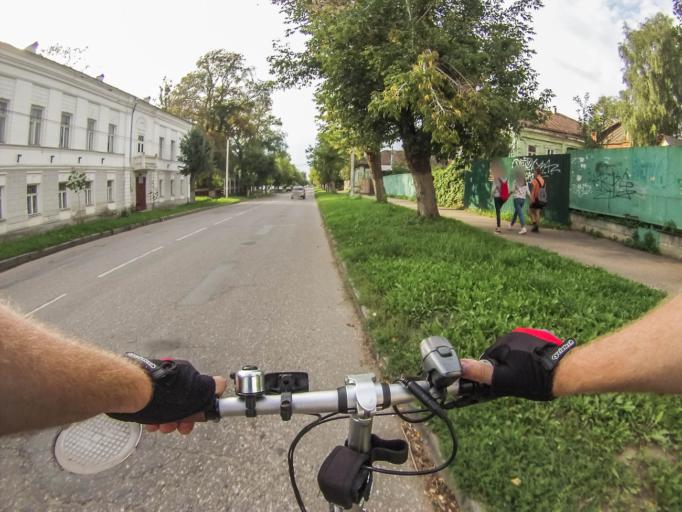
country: RU
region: Kostroma
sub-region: Kostromskoy Rayon
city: Kostroma
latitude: 57.7715
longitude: 40.9147
